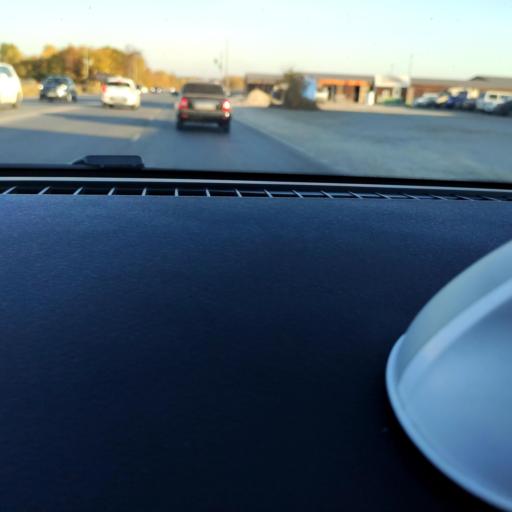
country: RU
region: Samara
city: Petra-Dubrava
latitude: 53.2724
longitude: 50.2717
